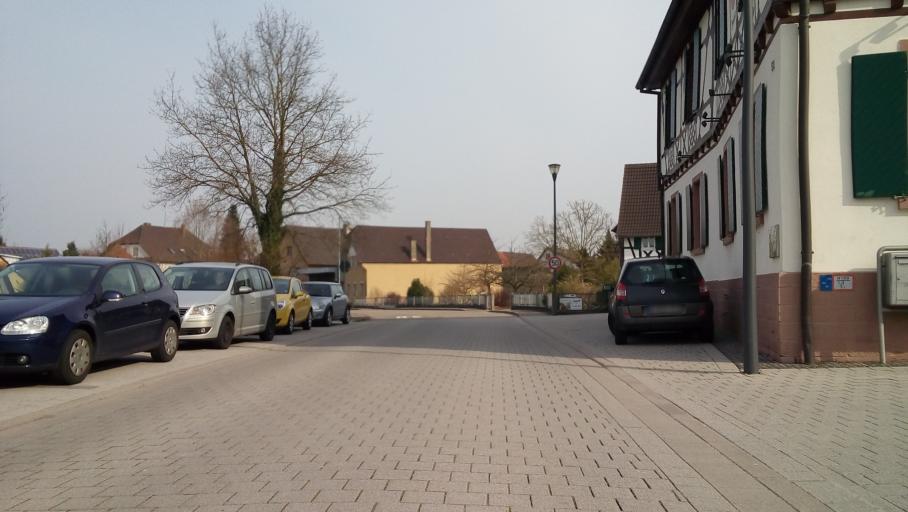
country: DE
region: Baden-Wuerttemberg
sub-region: Freiburg Region
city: Rheinau
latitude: 48.6676
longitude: 7.9355
